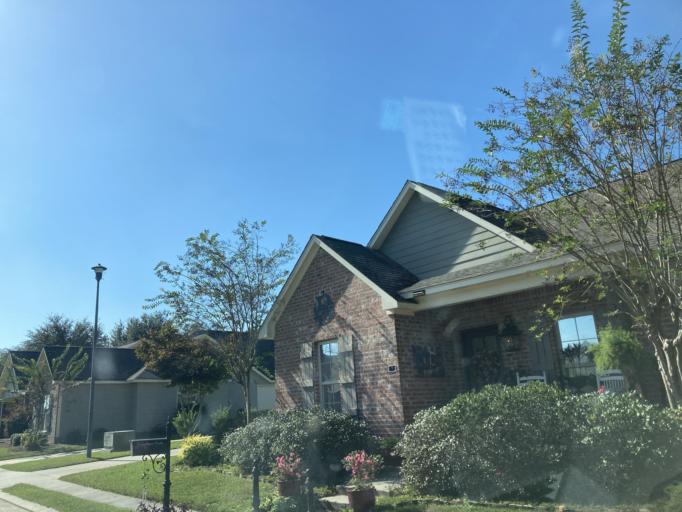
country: US
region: Mississippi
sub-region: Lamar County
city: West Hattiesburg
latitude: 31.3146
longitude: -89.4843
